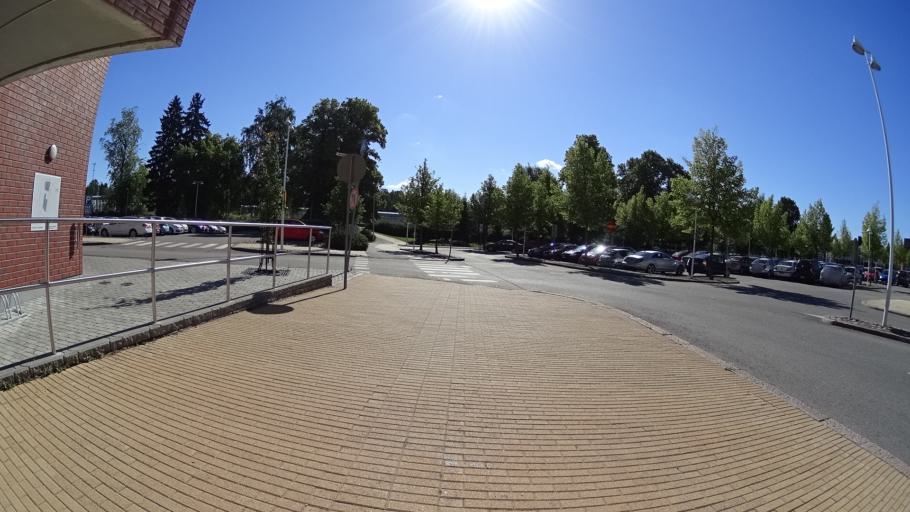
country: FI
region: Uusimaa
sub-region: Helsinki
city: Kerava
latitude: 60.4062
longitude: 25.1050
